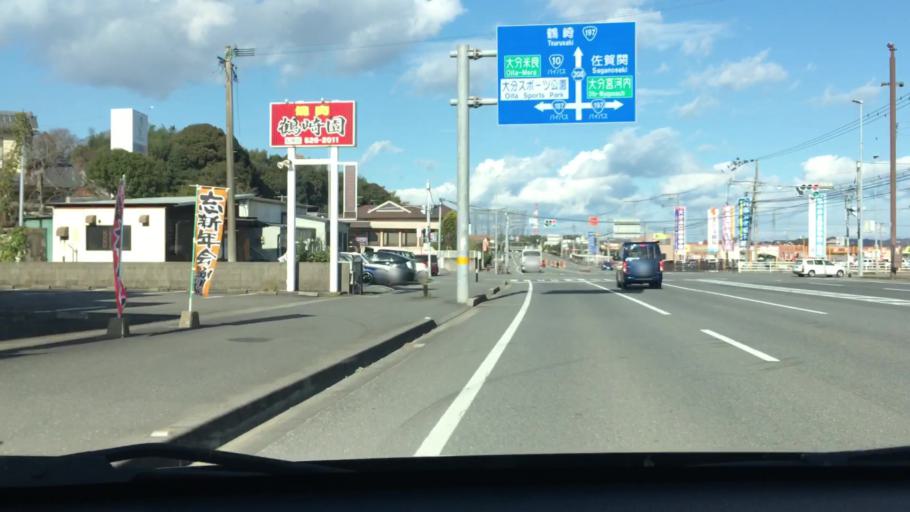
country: JP
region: Oita
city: Tsurusaki
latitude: 33.1896
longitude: 131.6712
